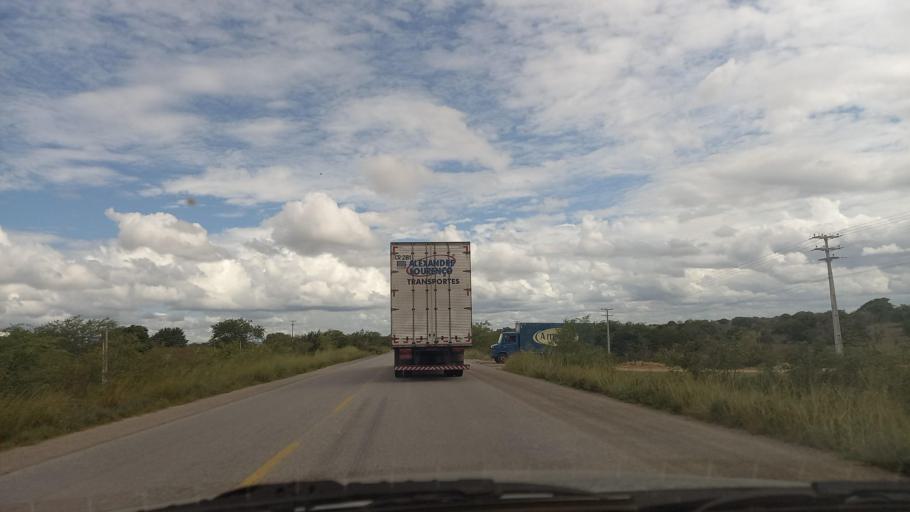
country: BR
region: Pernambuco
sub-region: Cachoeirinha
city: Cachoeirinha
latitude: -8.3921
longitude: -36.1790
